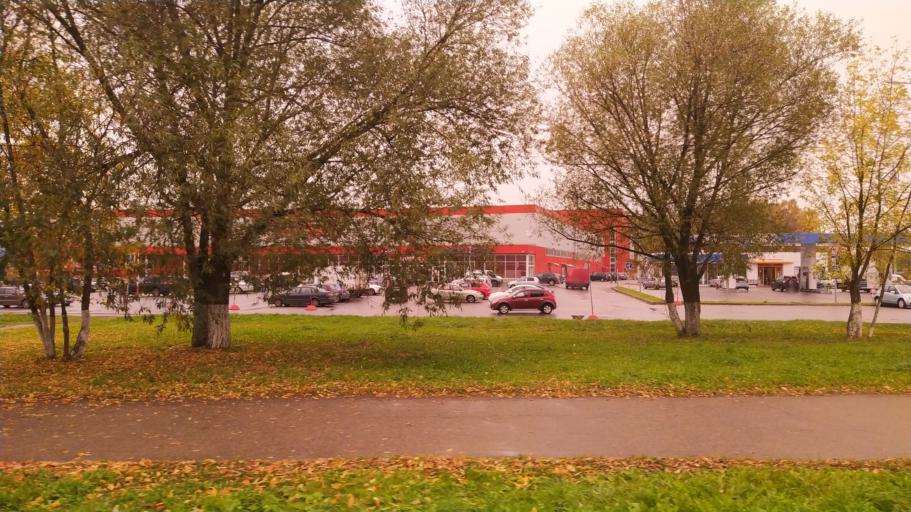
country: RU
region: Tverskaya
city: Tver
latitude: 56.8282
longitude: 35.8969
